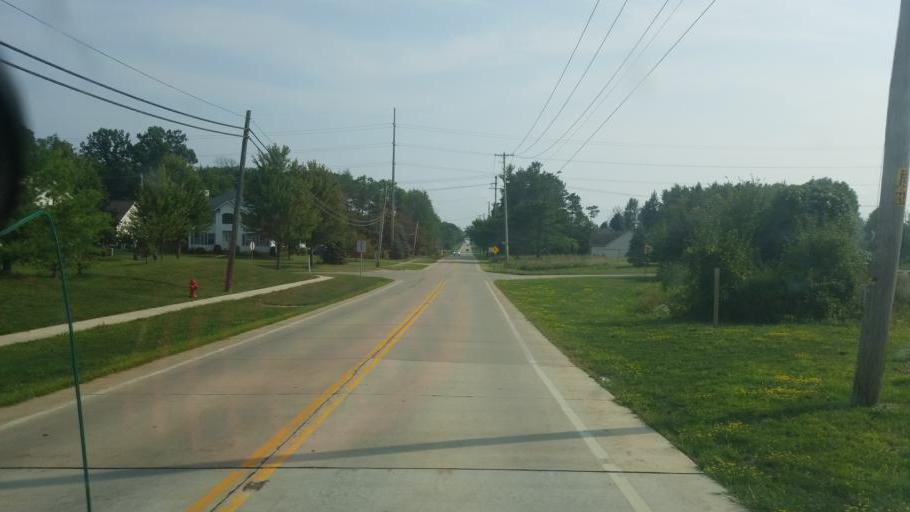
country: US
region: Ohio
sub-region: Medina County
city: Medina
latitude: 41.1211
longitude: -81.8840
